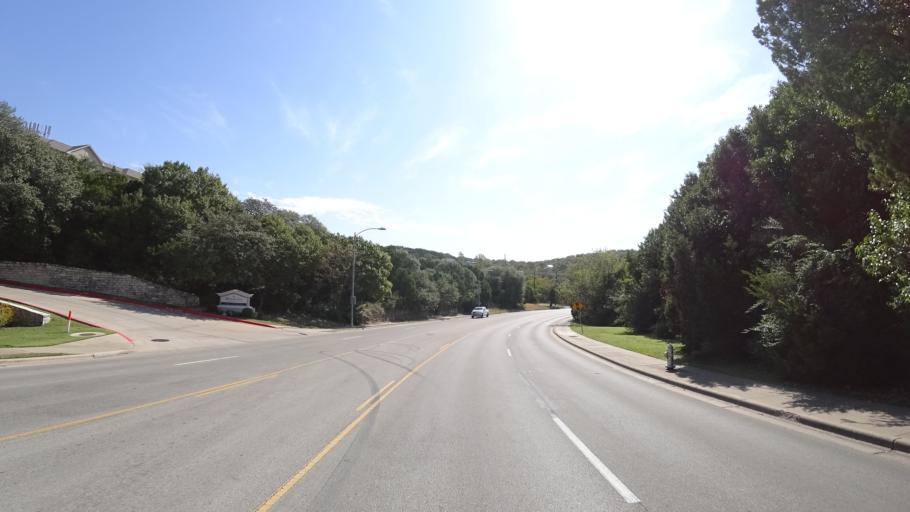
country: US
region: Texas
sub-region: Travis County
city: West Lake Hills
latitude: 30.3425
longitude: -97.7703
